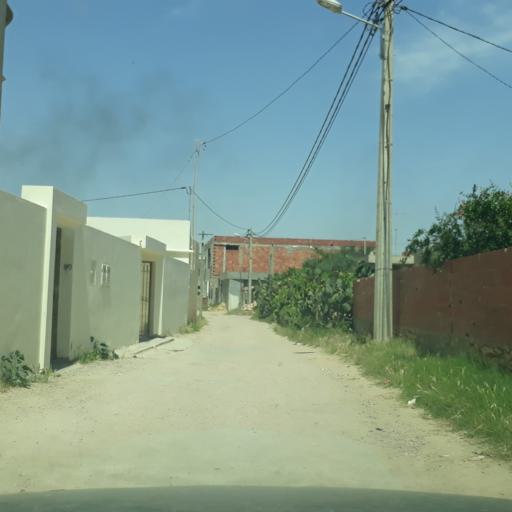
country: TN
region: Safaqis
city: Al Qarmadah
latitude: 34.8229
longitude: 10.7793
